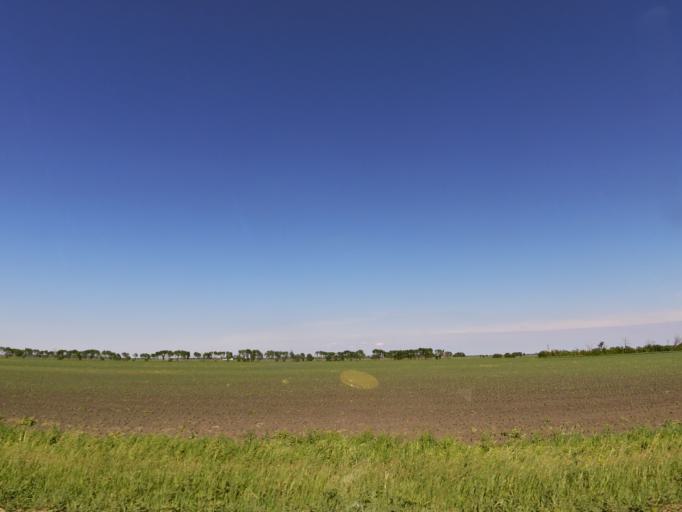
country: US
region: North Dakota
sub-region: Walsh County
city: Grafton
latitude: 48.3912
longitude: -97.2777
